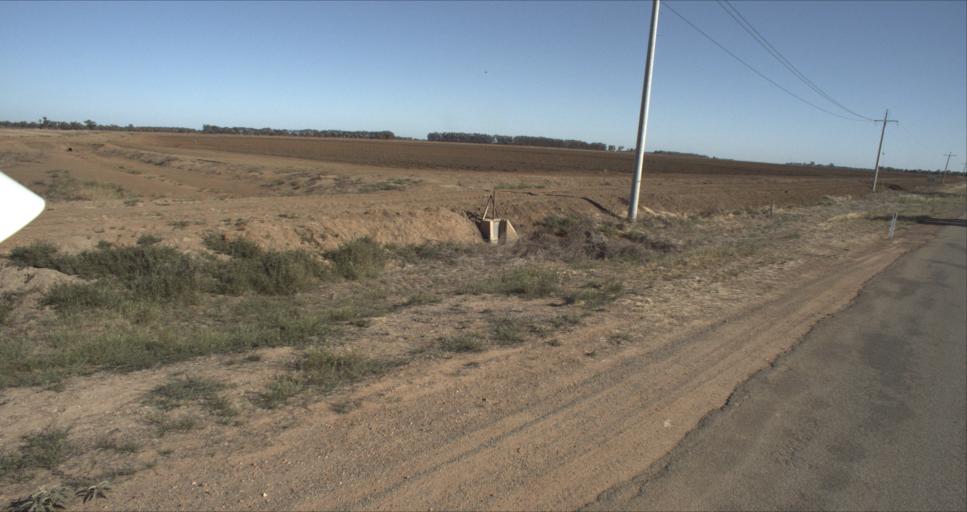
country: AU
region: New South Wales
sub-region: Leeton
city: Leeton
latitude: -34.6046
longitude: 146.2570
